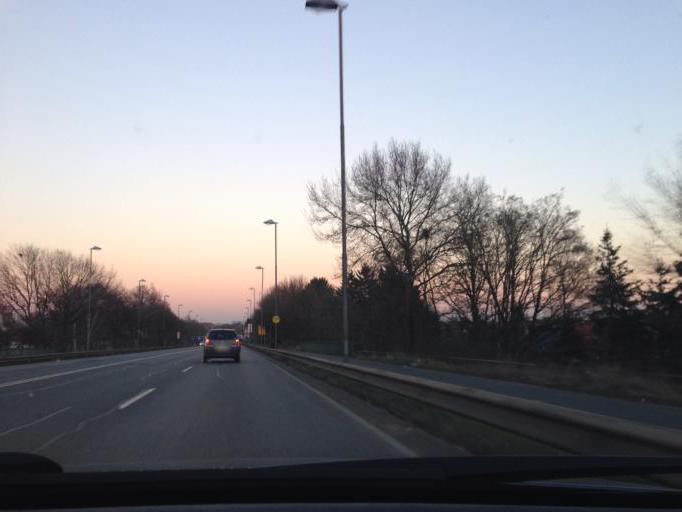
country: DE
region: Lower Saxony
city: Celle
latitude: 52.6069
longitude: 10.0591
